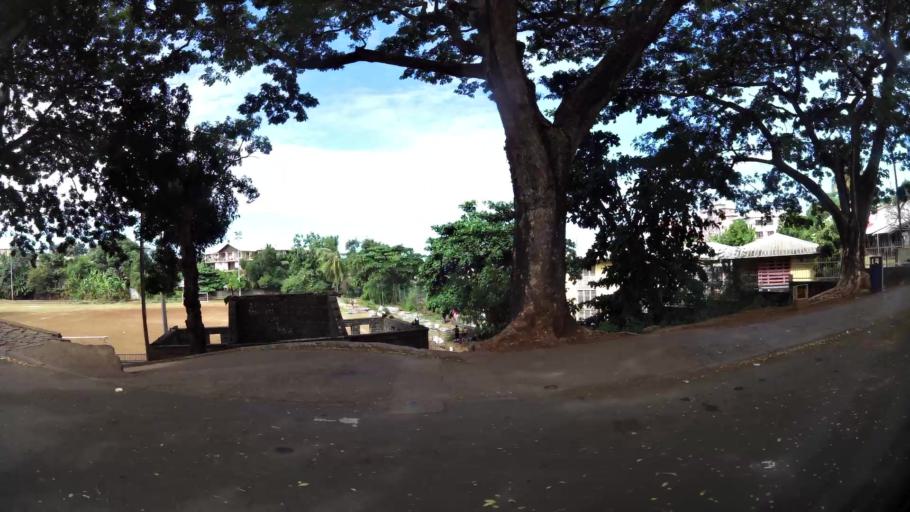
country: YT
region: Mamoudzou
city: Mamoudzou
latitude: -12.7819
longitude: 45.2274
